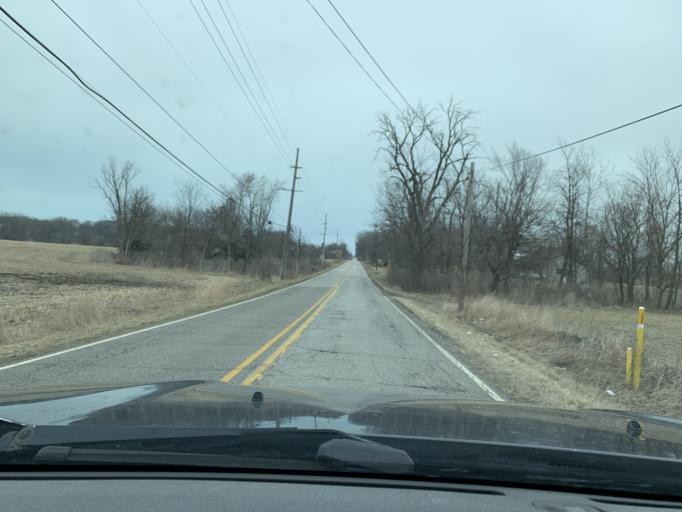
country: US
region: Indiana
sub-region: Porter County
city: Chesterton
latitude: 41.5665
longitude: -87.0665
